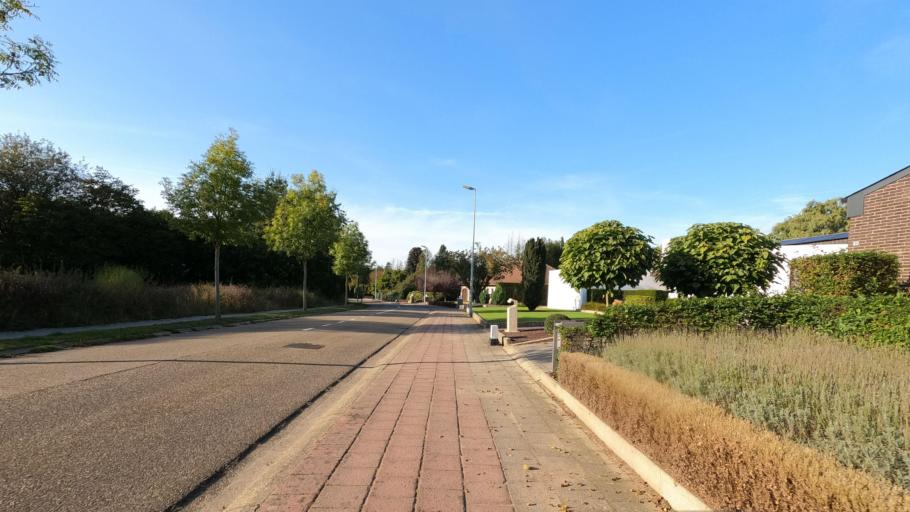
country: BE
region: Flanders
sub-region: Provincie Antwerpen
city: Heist-op-den-Berg
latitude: 51.0853
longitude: 4.7177
